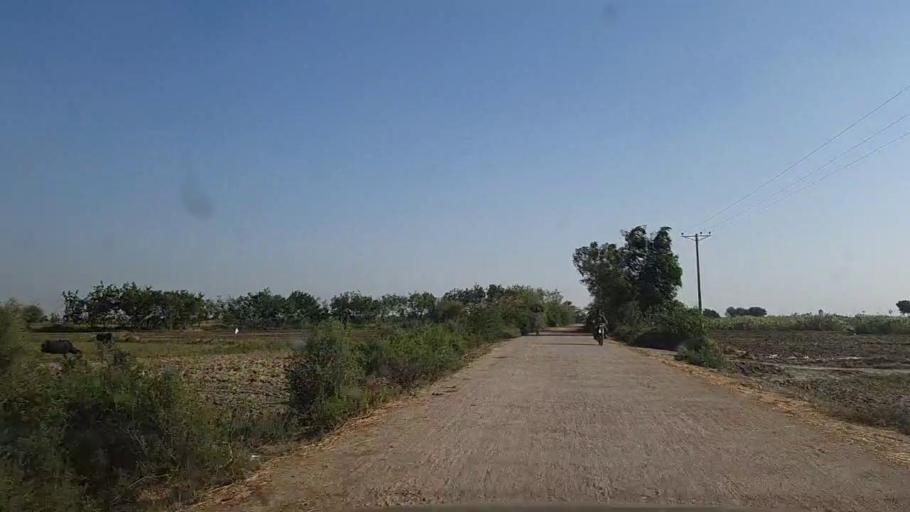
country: PK
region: Sindh
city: Daro Mehar
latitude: 24.6330
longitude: 68.0775
